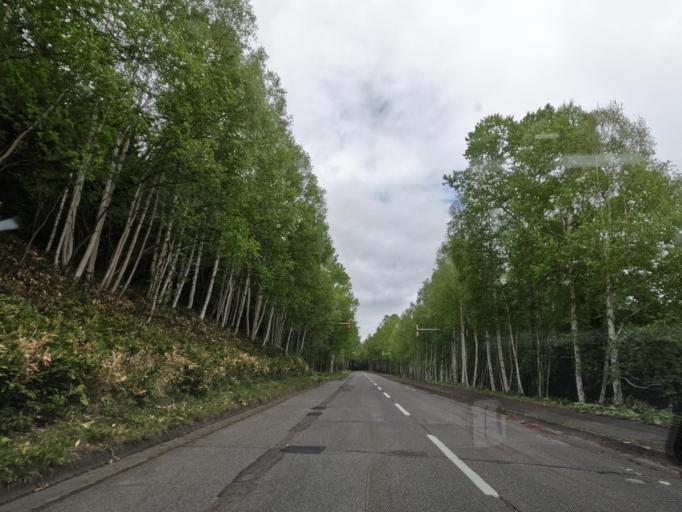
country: JP
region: Hokkaido
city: Kamikawa
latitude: 43.6499
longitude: 143.0301
